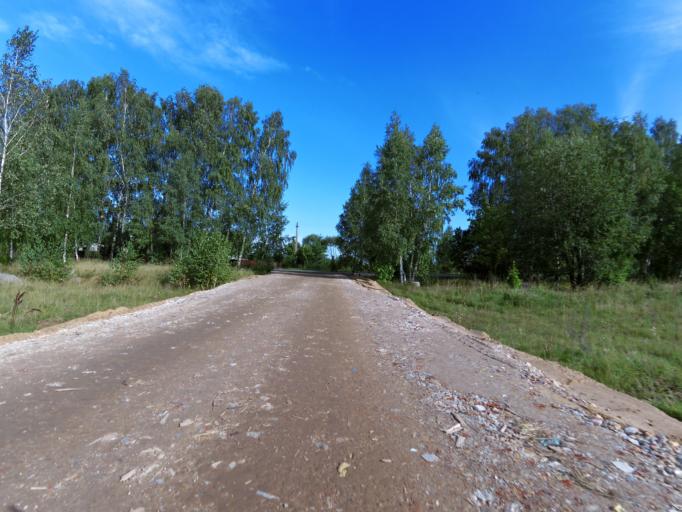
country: LT
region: Vilnius County
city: Pilaite
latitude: 54.7101
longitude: 25.1703
